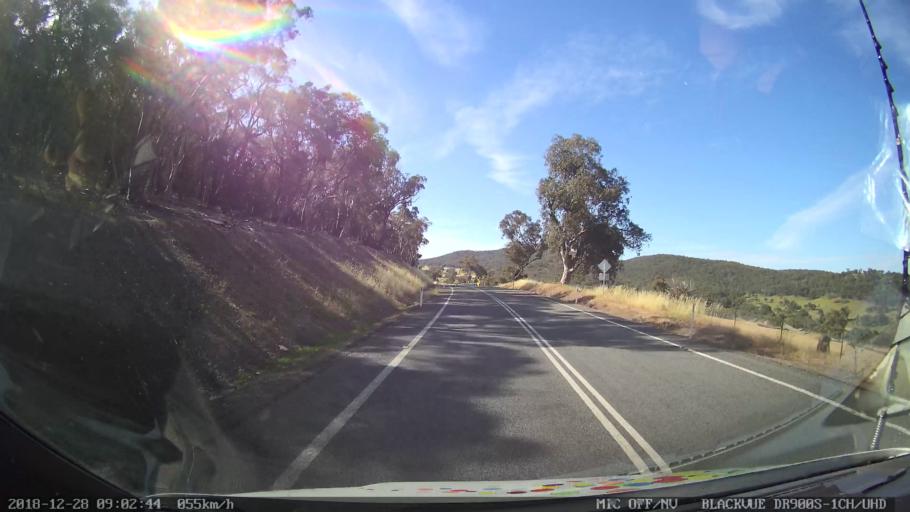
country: AU
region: New South Wales
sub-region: Upper Lachlan Shire
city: Crookwell
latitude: -34.1570
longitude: 149.3349
